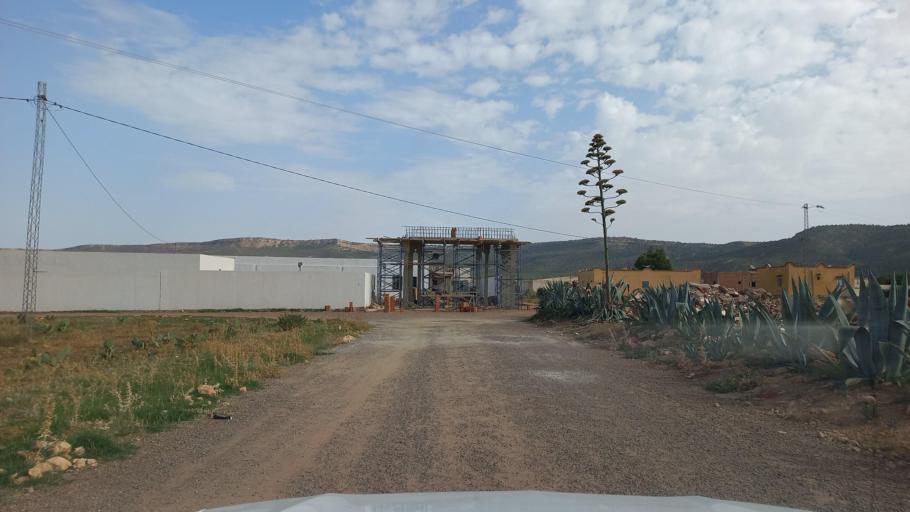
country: TN
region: Al Qasrayn
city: Kasserine
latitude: 35.3542
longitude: 8.8279
